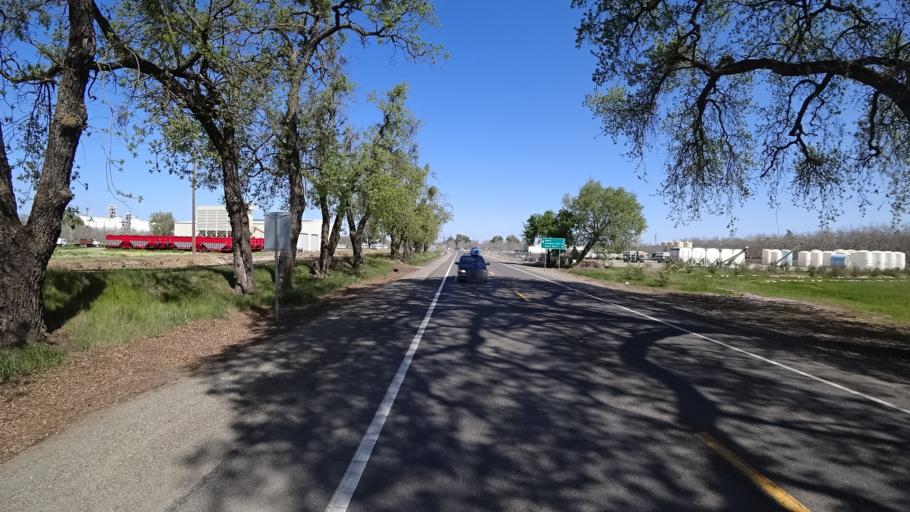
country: US
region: California
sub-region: Glenn County
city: Willows
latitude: 39.4555
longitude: -122.0174
